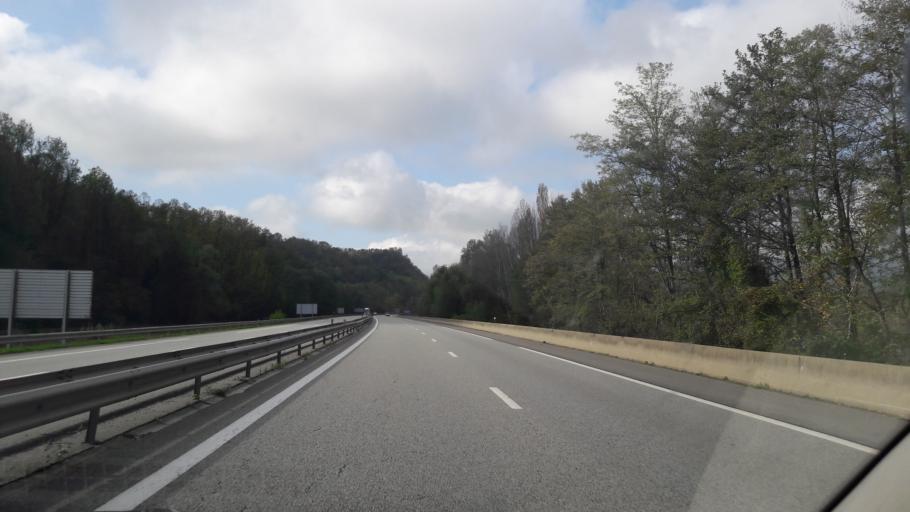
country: FR
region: Rhone-Alpes
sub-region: Departement de la Savoie
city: Coise-Saint-Jean-Pied-Gauthier
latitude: 45.5559
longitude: 6.1817
